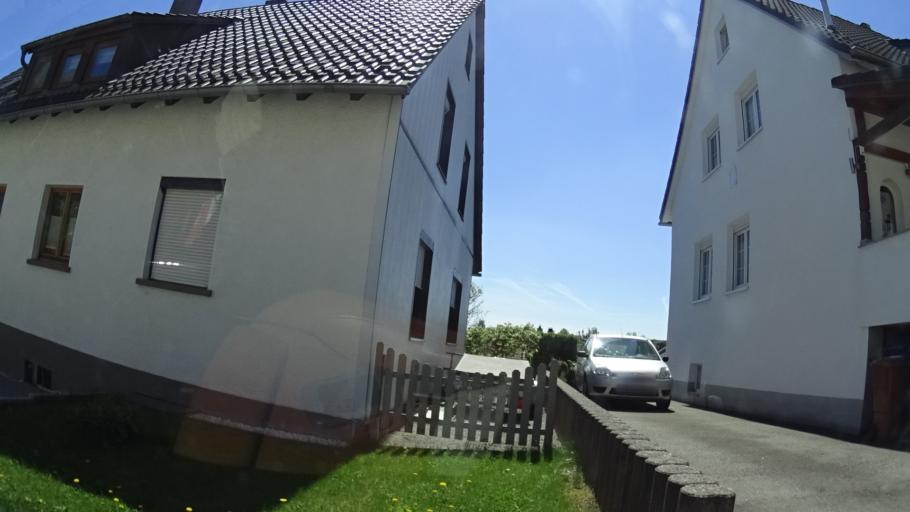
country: DE
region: Baden-Wuerttemberg
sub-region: Freiburg Region
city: Rottweil
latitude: 48.1698
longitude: 8.6153
